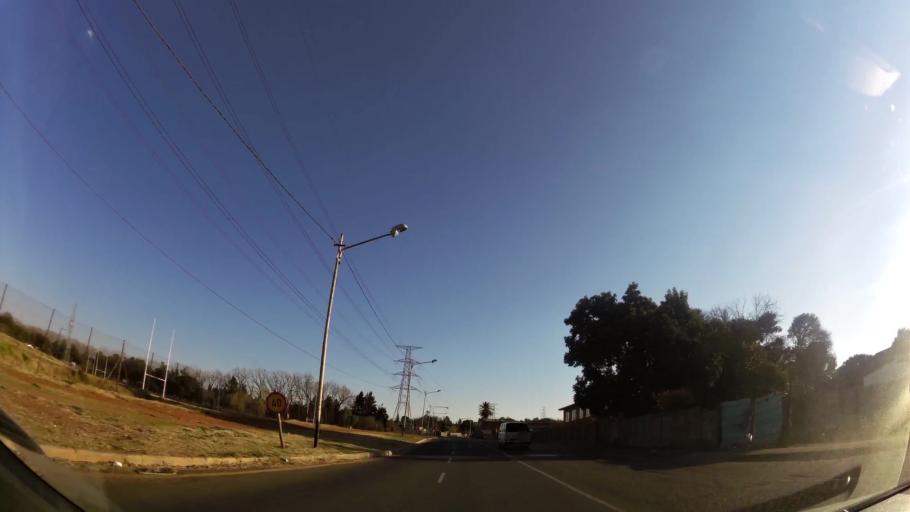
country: ZA
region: Gauteng
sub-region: Ekurhuleni Metropolitan Municipality
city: Germiston
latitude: -26.1985
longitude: 28.1477
